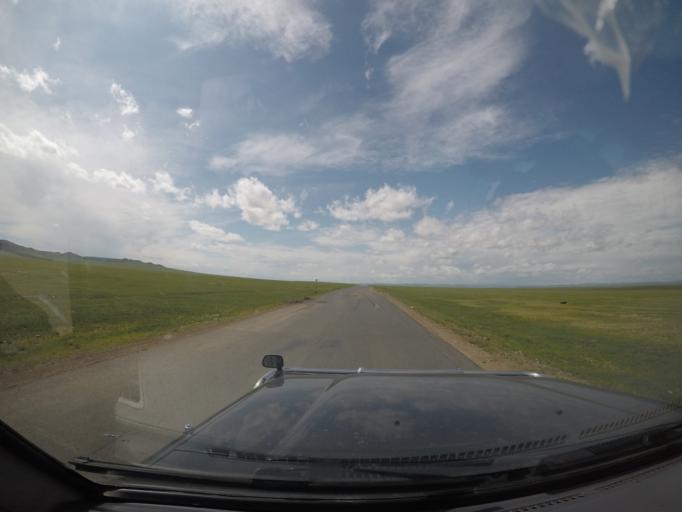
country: MN
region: Hentiy
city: Moron
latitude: 47.4150
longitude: 110.2080
